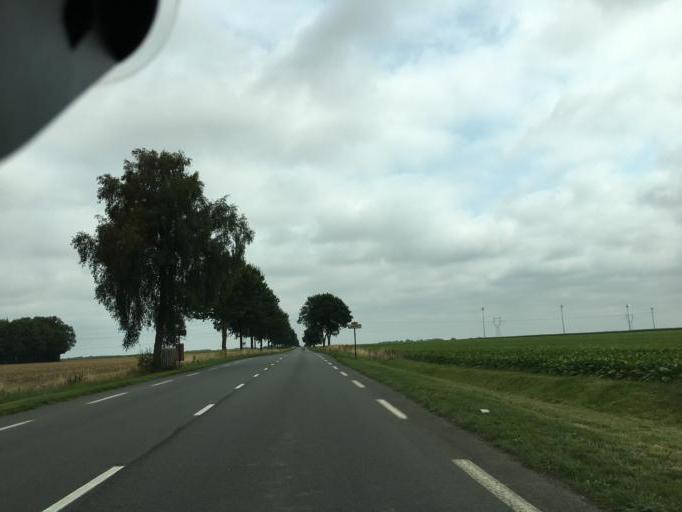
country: FR
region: Nord-Pas-de-Calais
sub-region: Departement du Pas-de-Calais
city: Saint-Pol-sur-Ternoise
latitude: 50.4126
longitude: 2.3804
